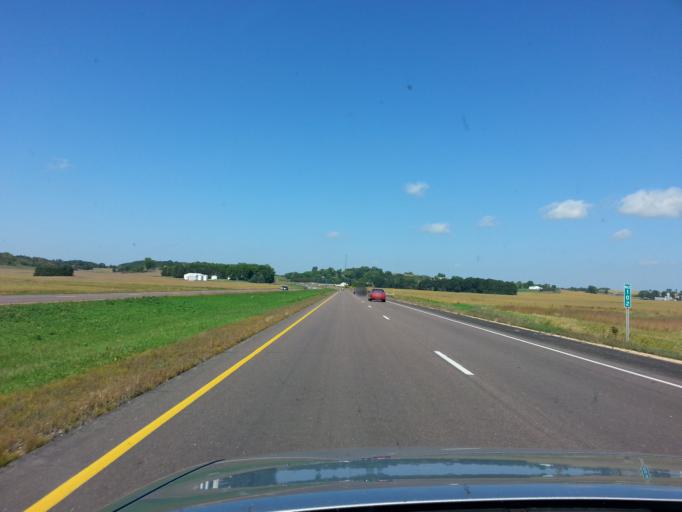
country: US
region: Minnesota
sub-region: Goodhue County
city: Cannon Falls
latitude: 44.5587
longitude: -92.9500
